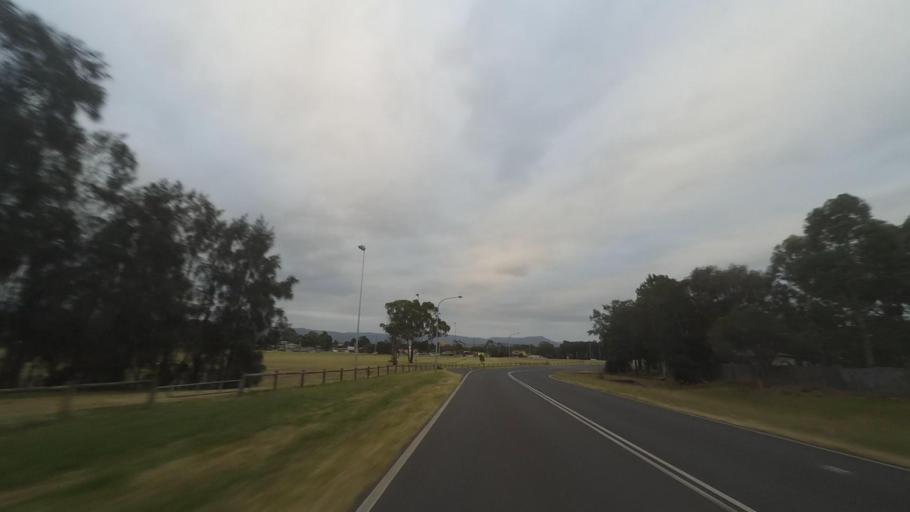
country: AU
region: New South Wales
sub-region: Shellharbour
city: Albion Park Rail
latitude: -34.5715
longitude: 150.8039
